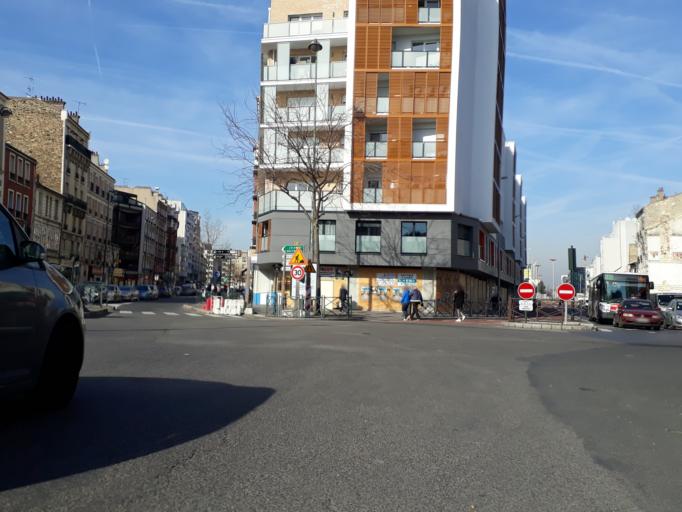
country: FR
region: Ile-de-France
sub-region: Departement des Hauts-de-Seine
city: Asnieres-sur-Seine
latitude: 48.9128
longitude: 2.2960
